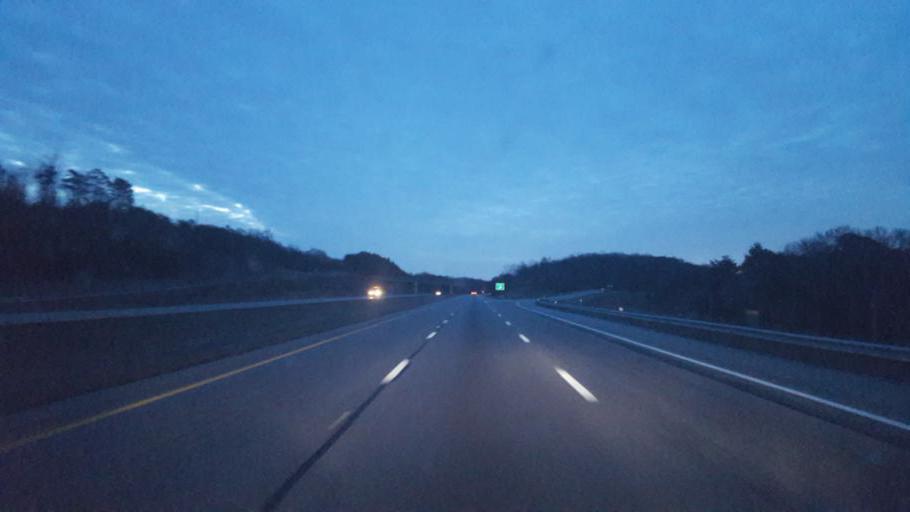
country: US
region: Ohio
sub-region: Jackson County
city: Jackson
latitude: 39.0969
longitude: -82.6638
